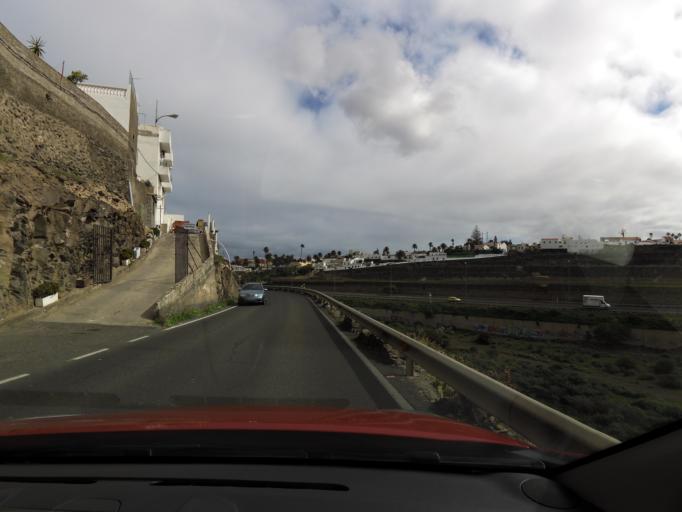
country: ES
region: Canary Islands
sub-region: Provincia de Las Palmas
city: Telde
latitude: 28.0054
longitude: -15.4198
